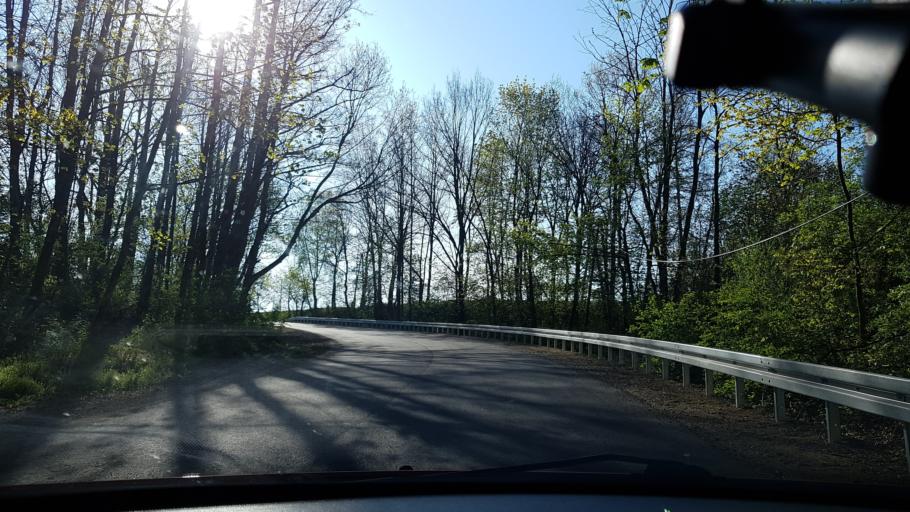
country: CZ
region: Olomoucky
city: Vidnava
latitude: 50.4195
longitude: 17.2123
